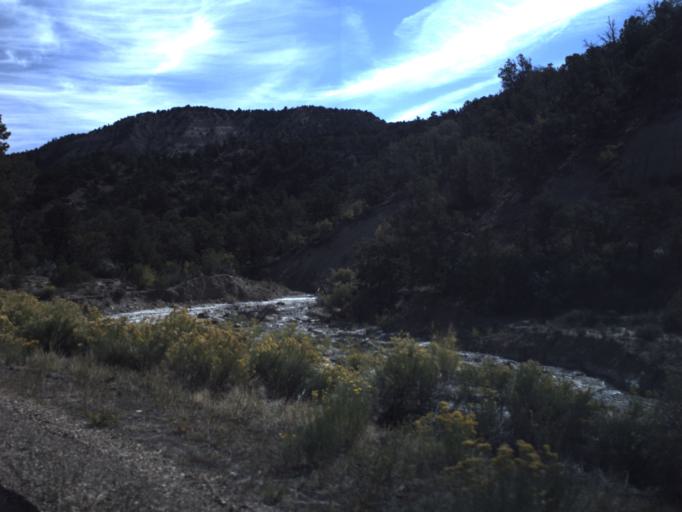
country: US
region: Utah
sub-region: Garfield County
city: Panguitch
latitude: 37.6217
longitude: -111.8610
